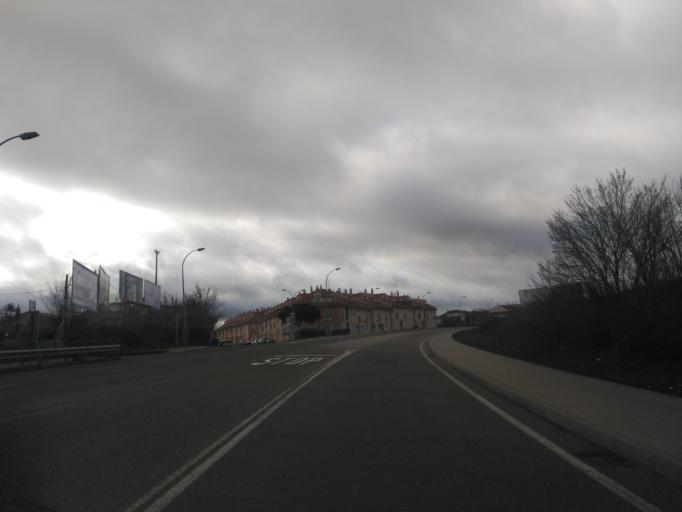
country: ES
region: Castille and Leon
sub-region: Provincia de Zamora
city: Morales del Vino
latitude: 41.4519
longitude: -5.7307
